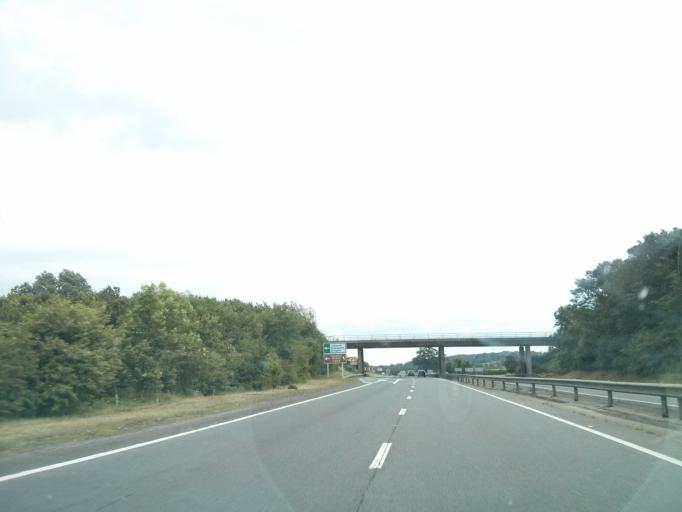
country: GB
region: England
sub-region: Bedford
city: Pertenhall
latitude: 52.3602
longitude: -0.4078
